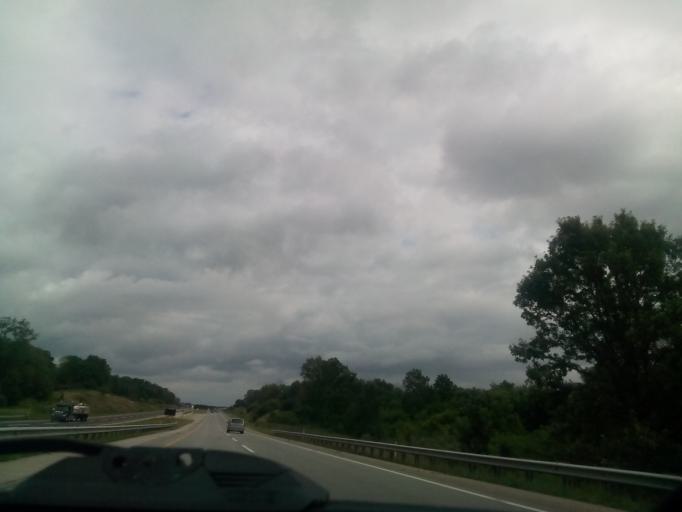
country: US
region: Indiana
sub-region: Steuben County
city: Fremont
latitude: 41.7088
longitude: -84.9363
